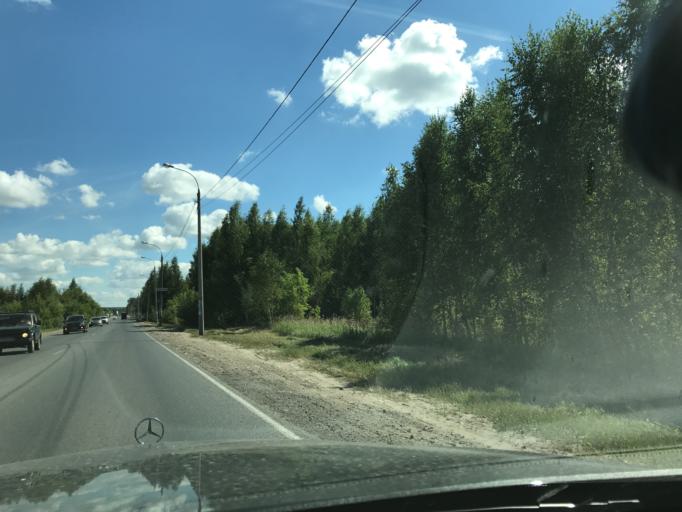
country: RU
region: Nizjnij Novgorod
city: Gorbatovka
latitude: 56.2159
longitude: 43.7585
